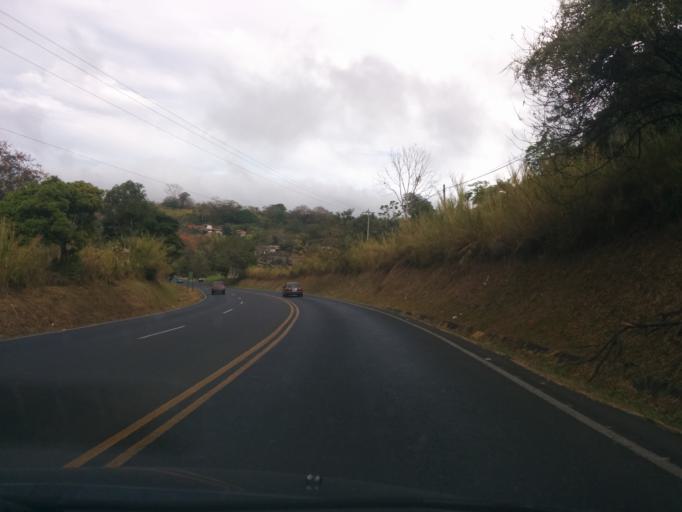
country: CR
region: Alajuela
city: San Ramon
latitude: 10.0787
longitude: -84.4579
